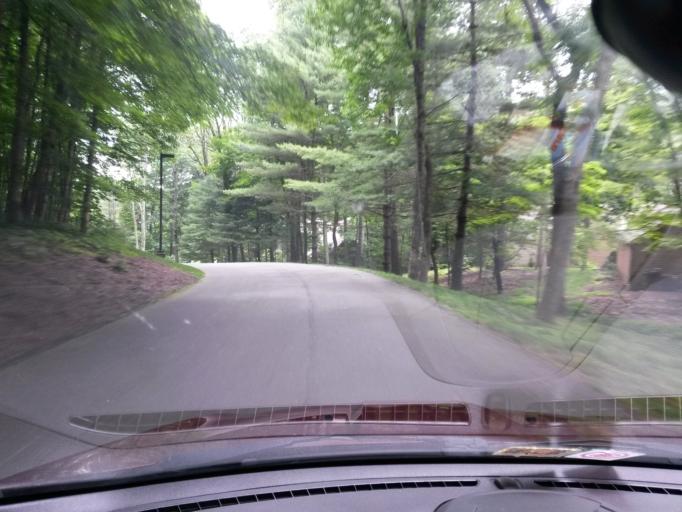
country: US
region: Virginia
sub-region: Bath County
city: Warm Springs
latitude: 38.0042
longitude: -79.8184
